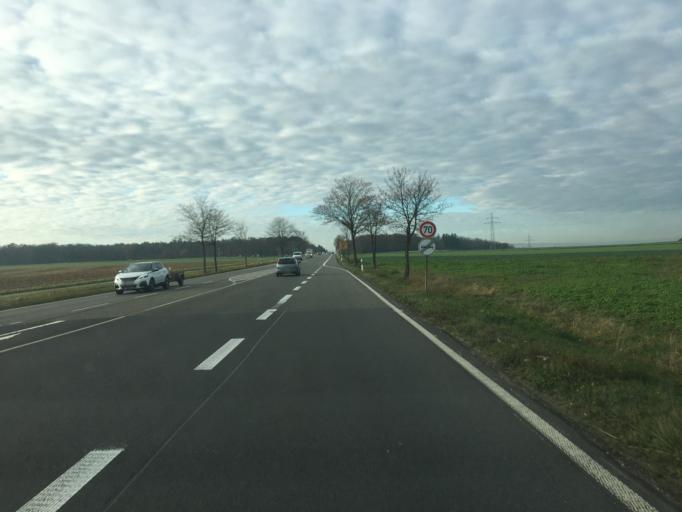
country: DE
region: North Rhine-Westphalia
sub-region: Regierungsbezirk Koln
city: Euskirchen
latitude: 50.6474
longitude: 6.7201
